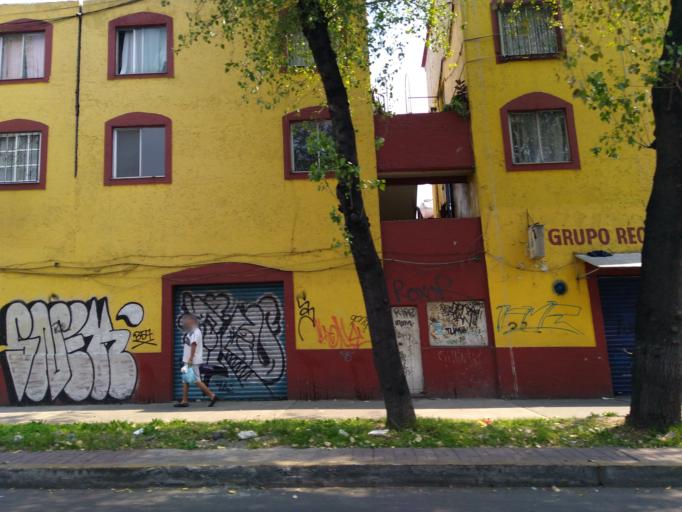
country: MX
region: Mexico City
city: Mexico City
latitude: 19.4416
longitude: -99.1177
